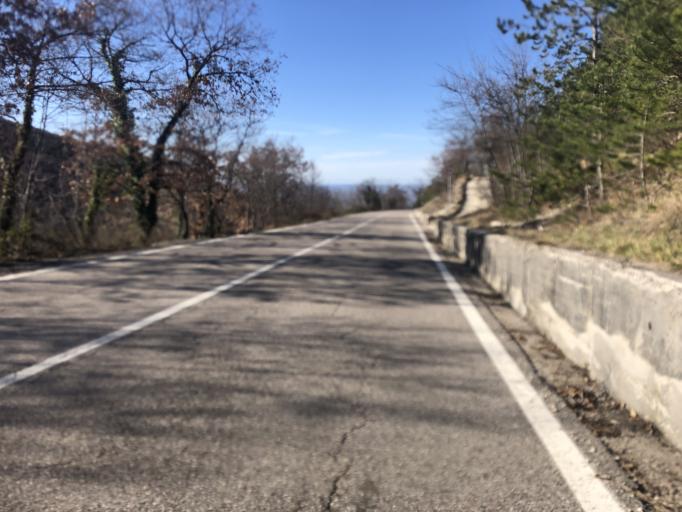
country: IT
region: Veneto
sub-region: Provincia di Verona
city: Fumane
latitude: 45.5652
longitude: 10.8593
